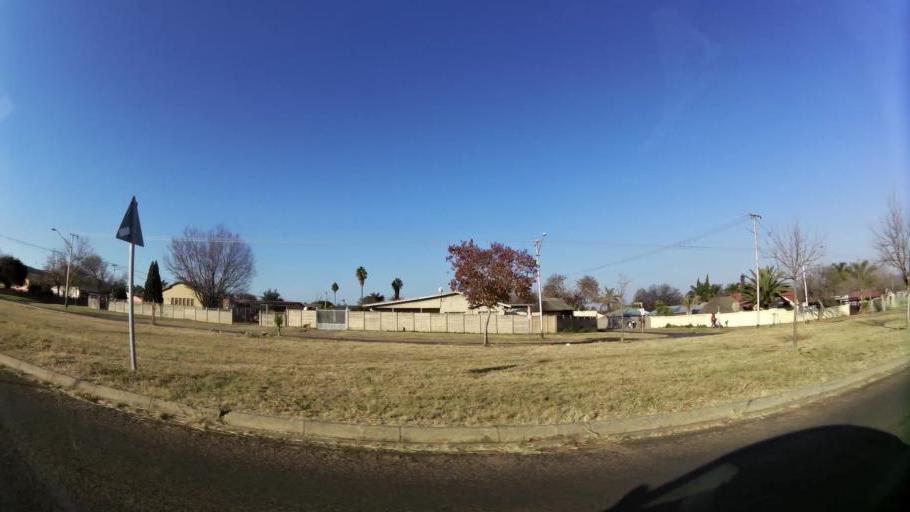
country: ZA
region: Gauteng
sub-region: City of Tshwane Metropolitan Municipality
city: Pretoria
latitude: -25.7426
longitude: 28.1175
